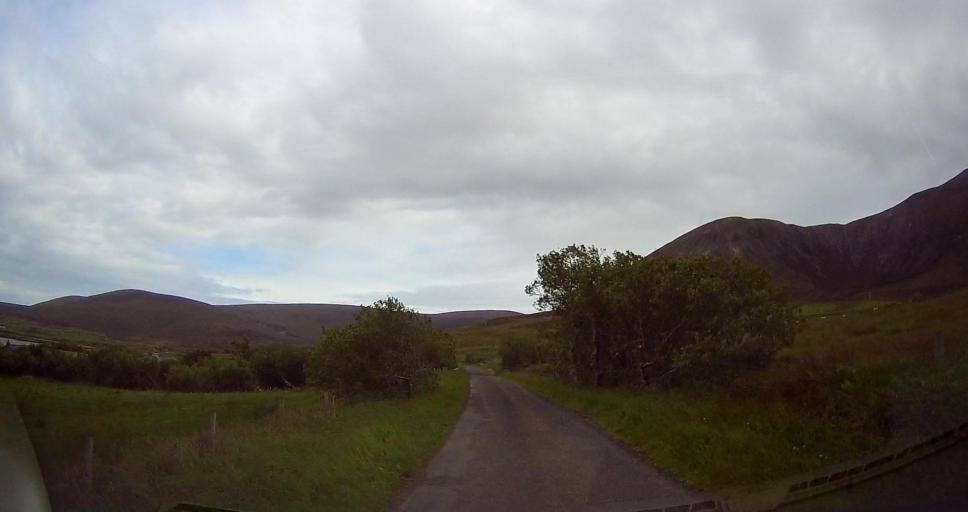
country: GB
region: Scotland
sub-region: Orkney Islands
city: Stromness
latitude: 58.9106
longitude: -3.3209
